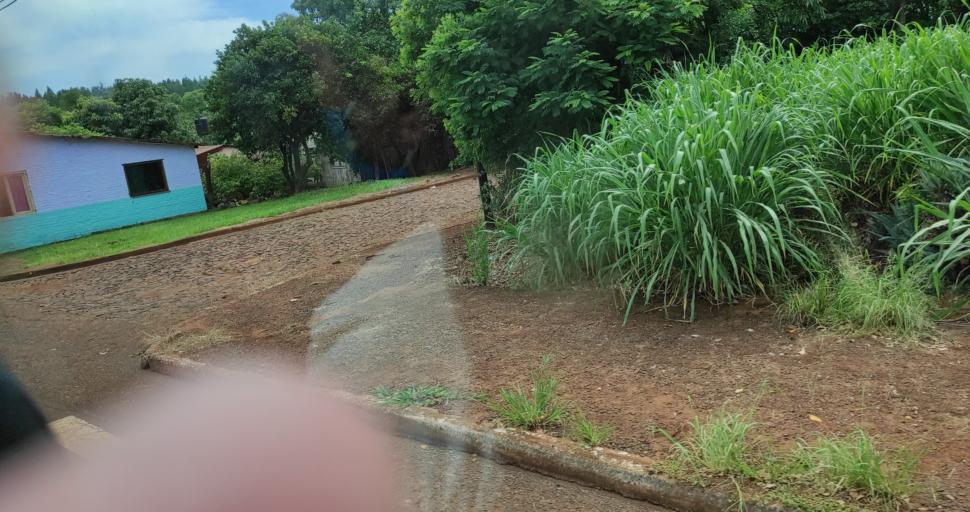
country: AR
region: Misiones
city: El Alcazar
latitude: -26.7100
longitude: -54.8162
